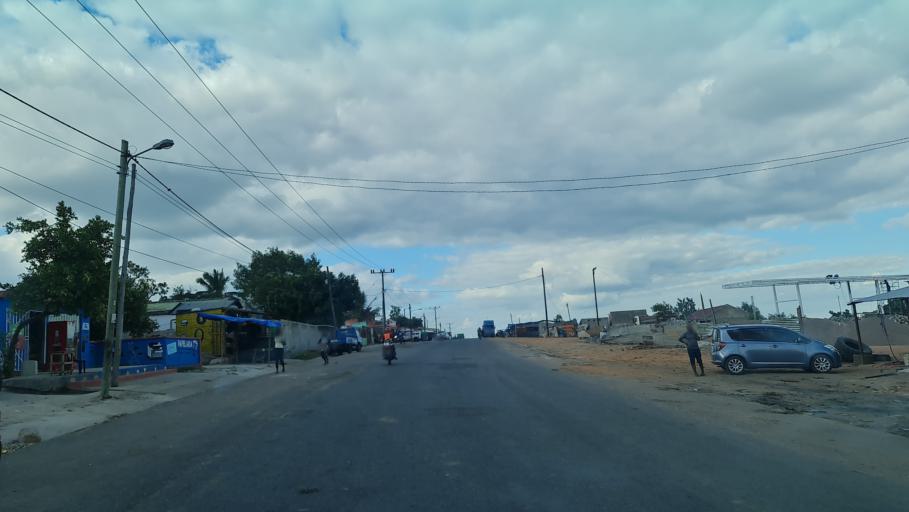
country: MZ
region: Manica
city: Chimoio
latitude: -19.2103
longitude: 33.9264
